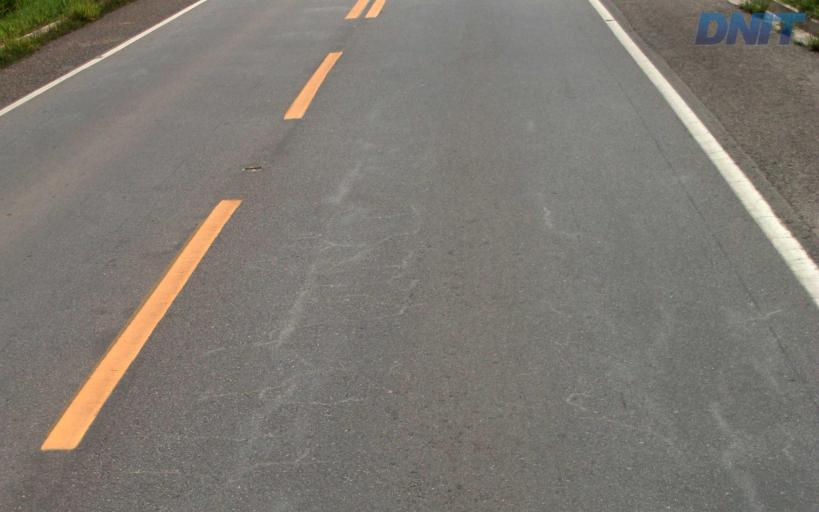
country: BR
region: Minas Gerais
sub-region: Belo Oriente
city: Belo Oriente
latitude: -19.1167
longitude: -42.2104
